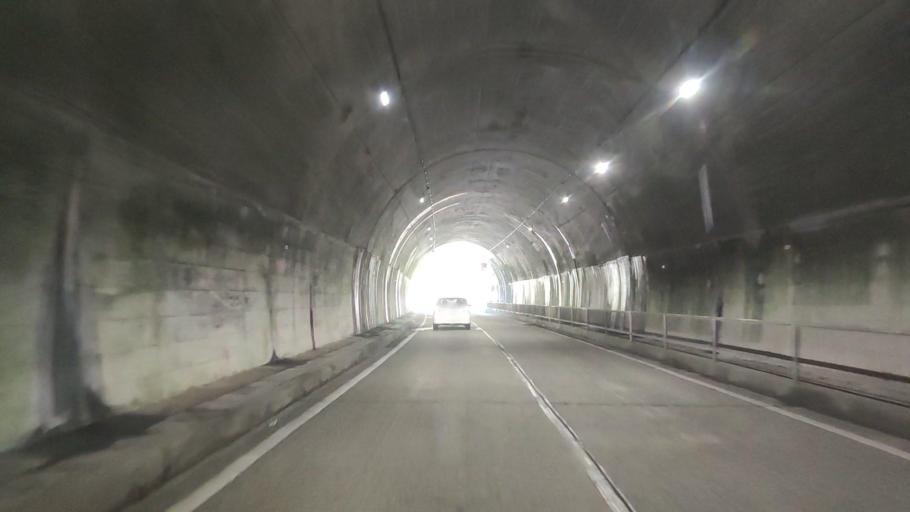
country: JP
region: Mie
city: Owase
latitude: 34.1759
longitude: 136.0034
